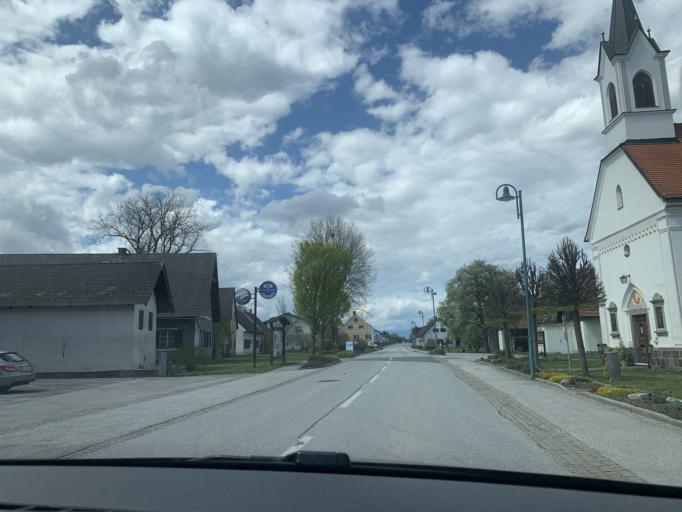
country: AT
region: Styria
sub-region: Politischer Bezirk Graz-Umgebung
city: Wundschuh
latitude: 46.9092
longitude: 15.4146
